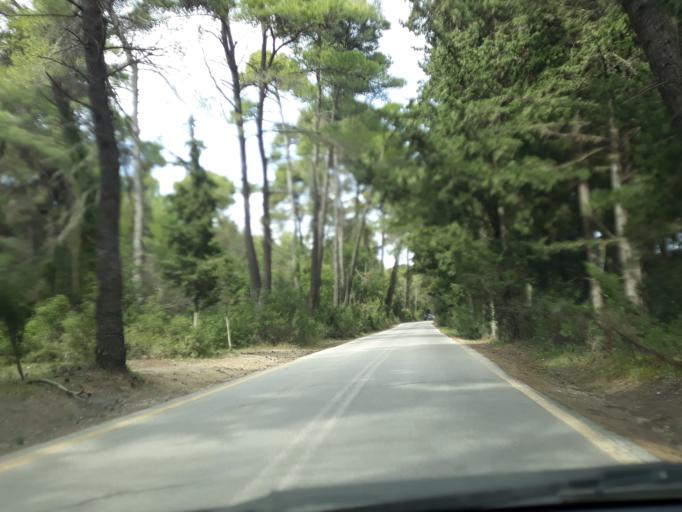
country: GR
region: Attica
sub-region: Nomarchia Anatolikis Attikis
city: Varybobi
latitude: 38.1575
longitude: 23.7914
